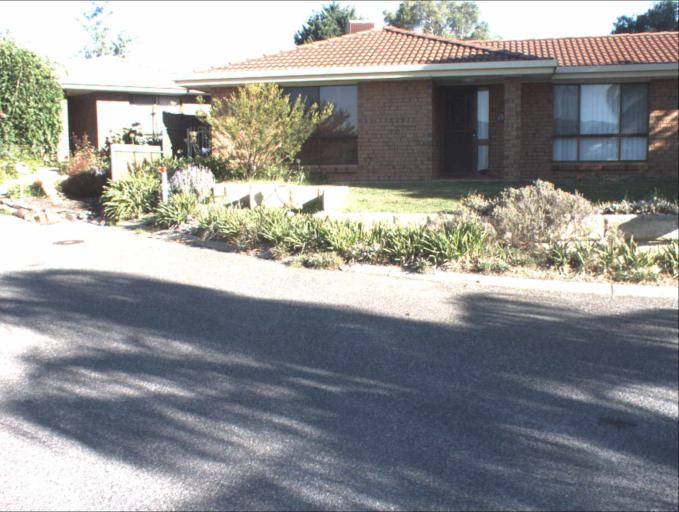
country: AU
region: South Australia
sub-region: Campbelltown
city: Paradise
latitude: -34.8715
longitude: 138.6535
